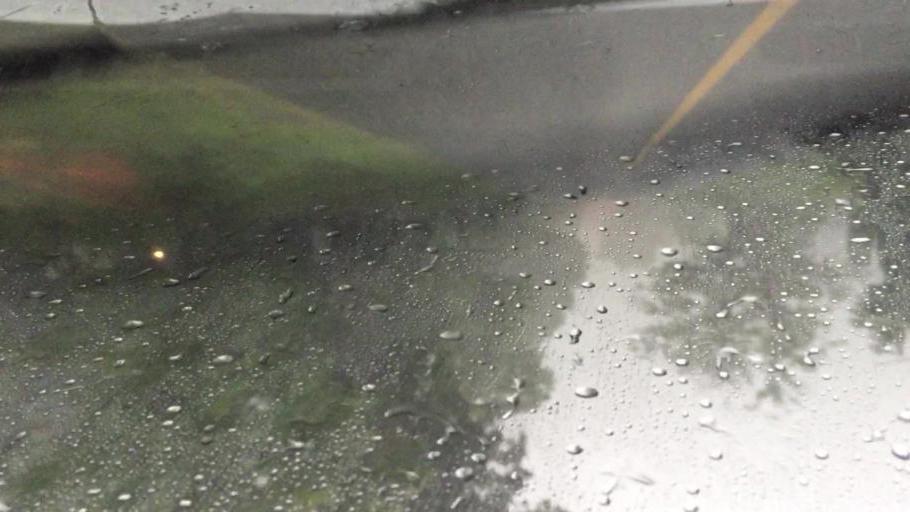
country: CA
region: Ontario
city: Markham
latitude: 43.8561
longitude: -79.2036
